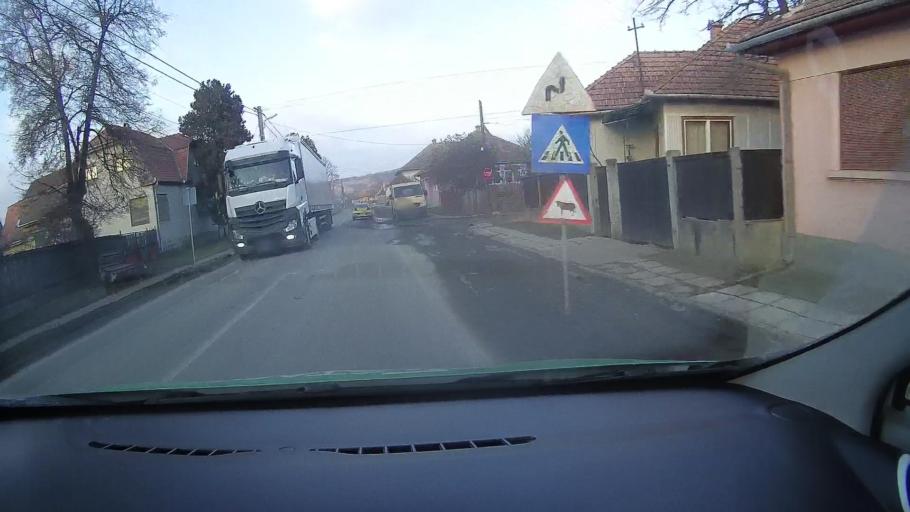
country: RO
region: Harghita
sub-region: Oras Cristuru Secuiesc
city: Cristuru Secuiesc
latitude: 46.2835
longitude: 25.0246
